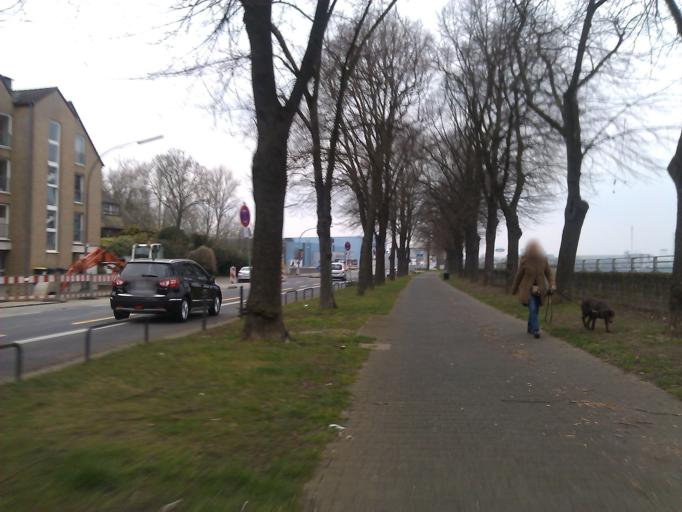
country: DE
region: North Rhine-Westphalia
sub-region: Regierungsbezirk Koln
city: Nippes
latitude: 50.9949
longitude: 6.9609
